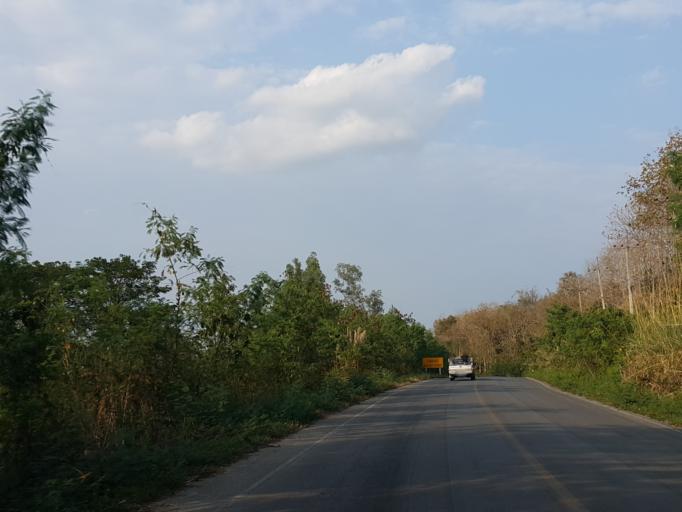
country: TH
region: Lampang
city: Lampang
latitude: 18.4682
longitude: 99.4623
